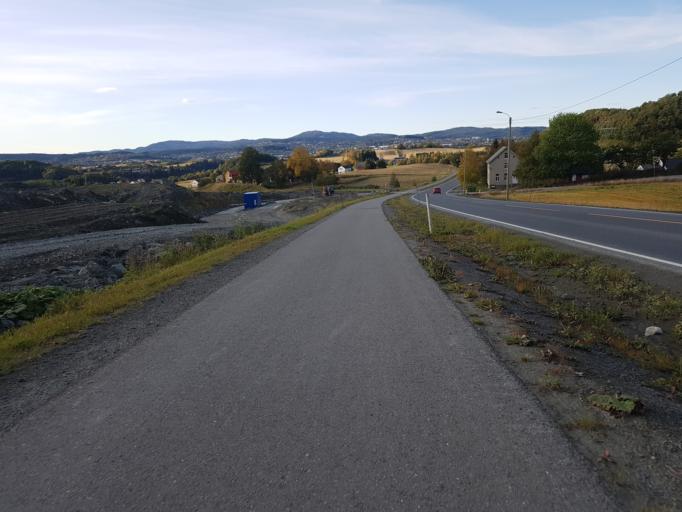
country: NO
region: Sor-Trondelag
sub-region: Trondheim
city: Trondheim
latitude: 63.3697
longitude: 10.4385
